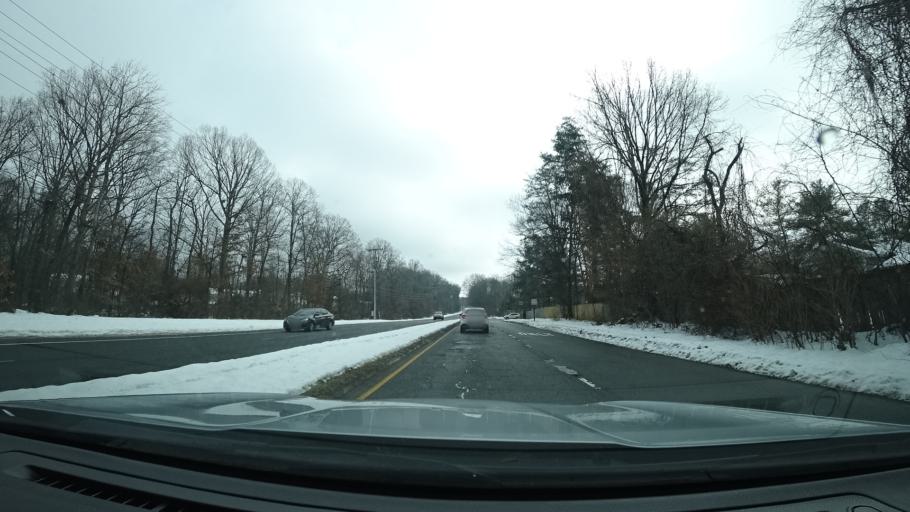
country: US
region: Virginia
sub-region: Fairfax County
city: Oak Hill
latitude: 38.9384
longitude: -77.3828
